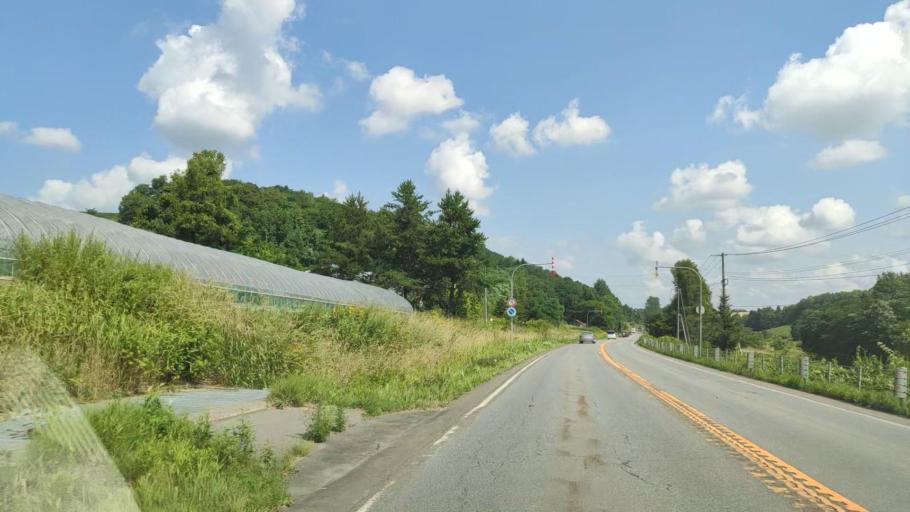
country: JP
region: Hokkaido
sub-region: Asahikawa-shi
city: Asahikawa
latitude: 43.5666
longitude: 142.4351
